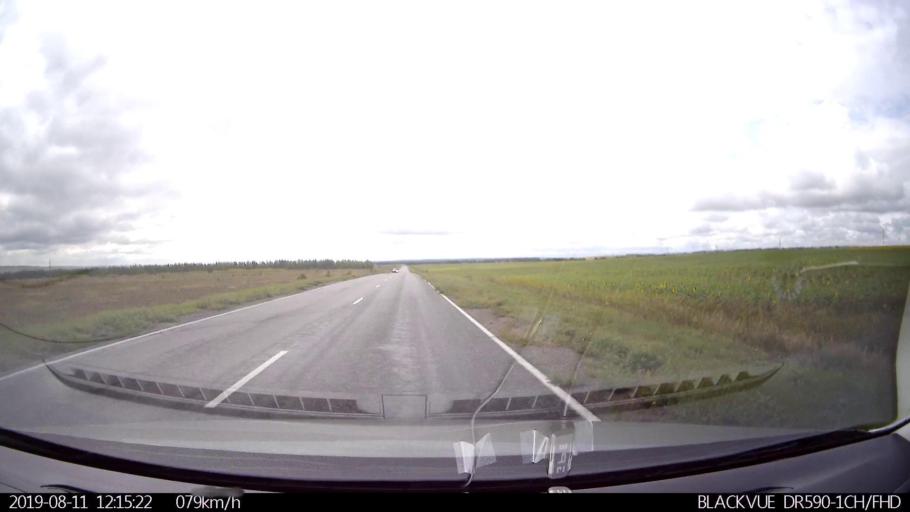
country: RU
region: Ulyanovsk
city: Ignatovka
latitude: 53.9424
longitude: 47.9692
